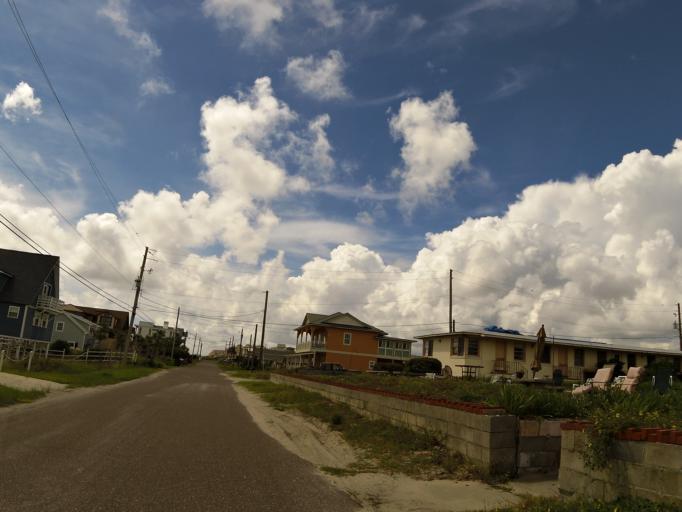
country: US
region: Florida
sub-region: Nassau County
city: Fernandina Beach
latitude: 30.5719
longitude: -81.4443
